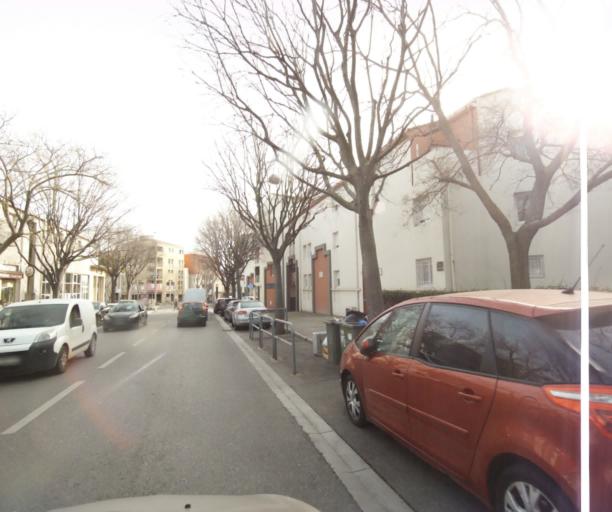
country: FR
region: Provence-Alpes-Cote d'Azur
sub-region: Departement des Bouches-du-Rhone
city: Les Pennes-Mirabeau
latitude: 43.4266
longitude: 5.2782
